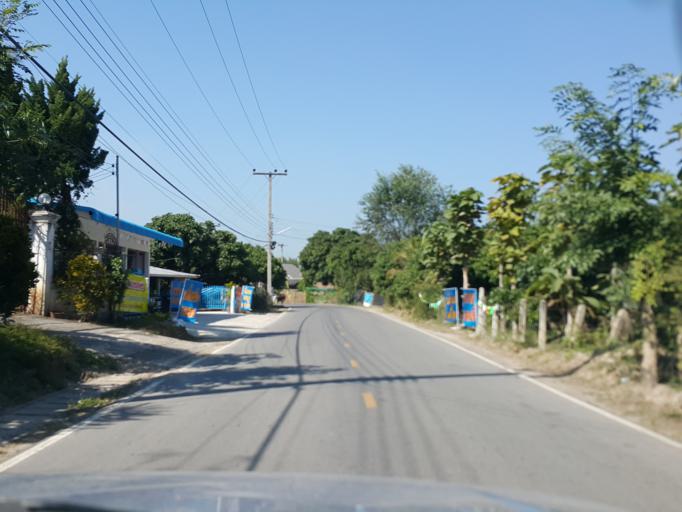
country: TH
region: Chiang Mai
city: Mae Wang
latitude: 18.5877
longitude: 98.8005
